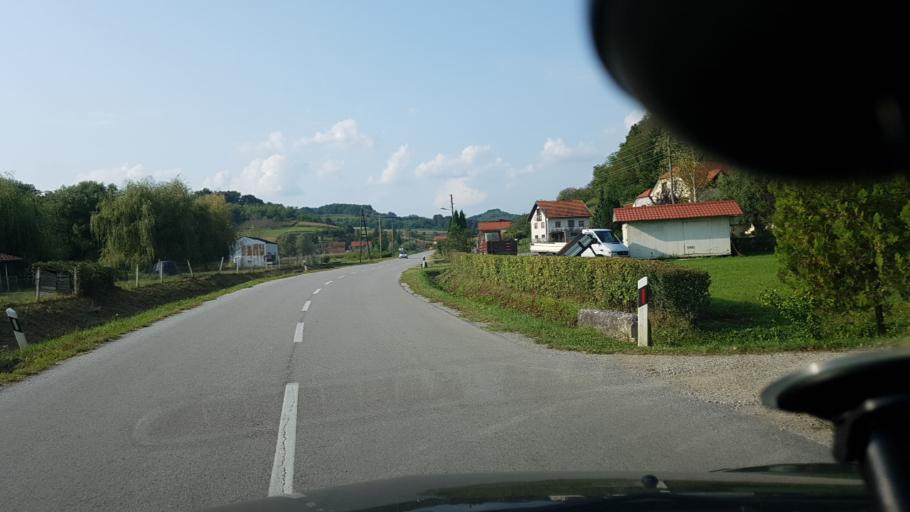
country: HR
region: Zagrebacka
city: Jakovlje
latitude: 46.0280
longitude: 15.7732
